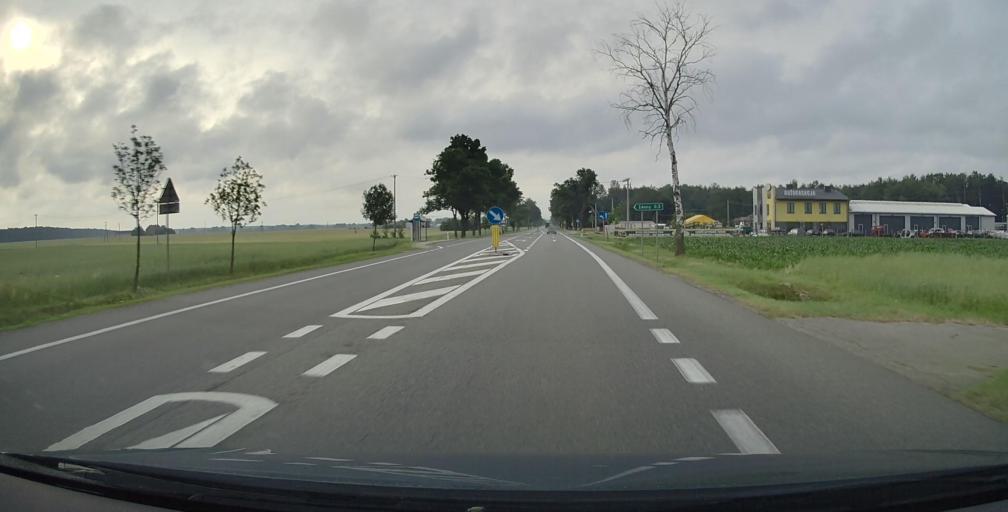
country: PL
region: Masovian Voivodeship
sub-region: Powiat siedlecki
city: Zbuczyn
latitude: 52.1004
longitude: 22.4051
